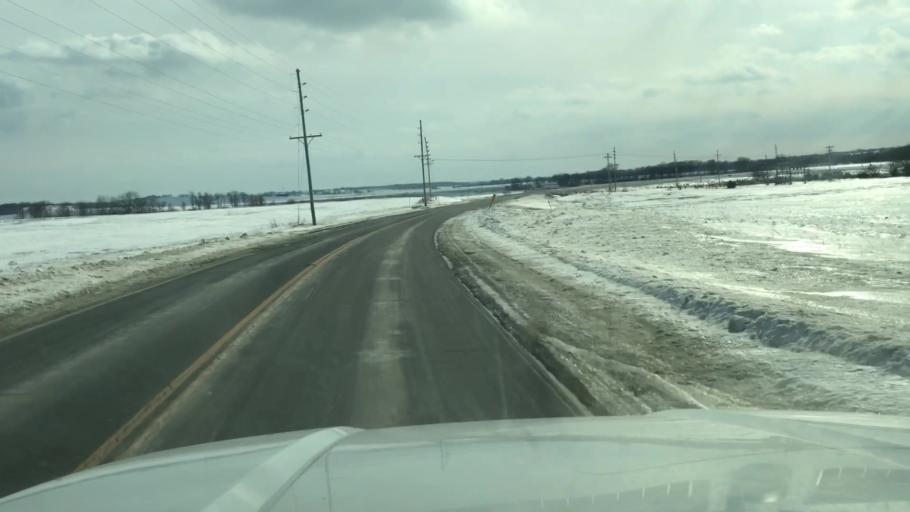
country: US
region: Missouri
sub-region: Gentry County
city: Stanberry
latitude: 40.3453
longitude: -94.6735
